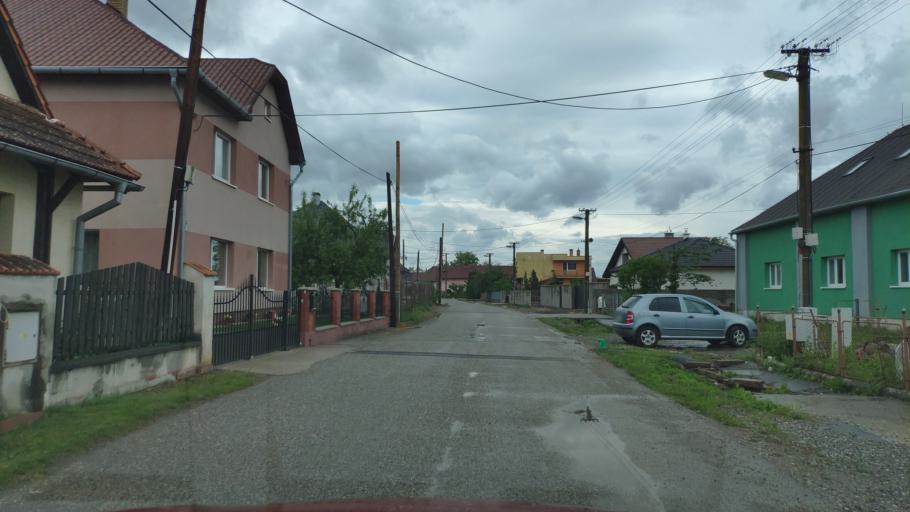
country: SK
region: Kosicky
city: Moldava nad Bodvou
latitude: 48.5715
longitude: 21.1218
